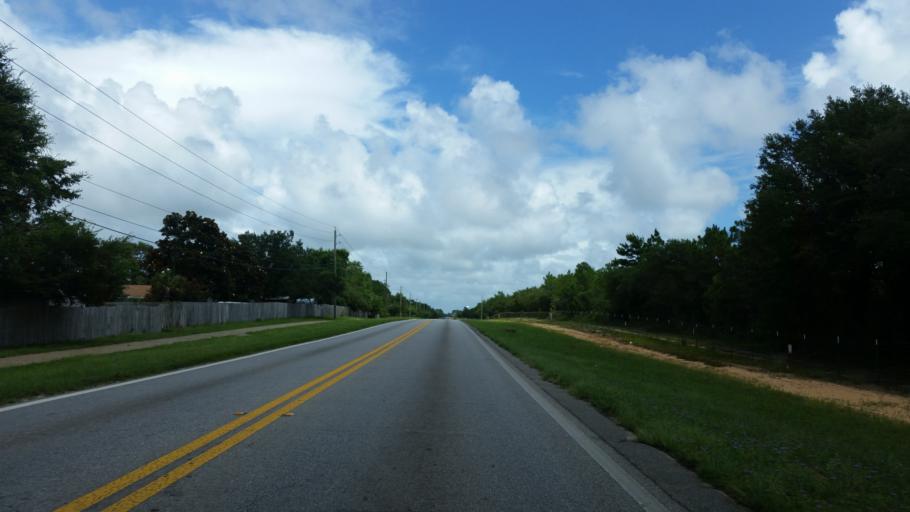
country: US
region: Florida
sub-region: Santa Rosa County
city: Holley
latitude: 30.4327
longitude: -86.8939
